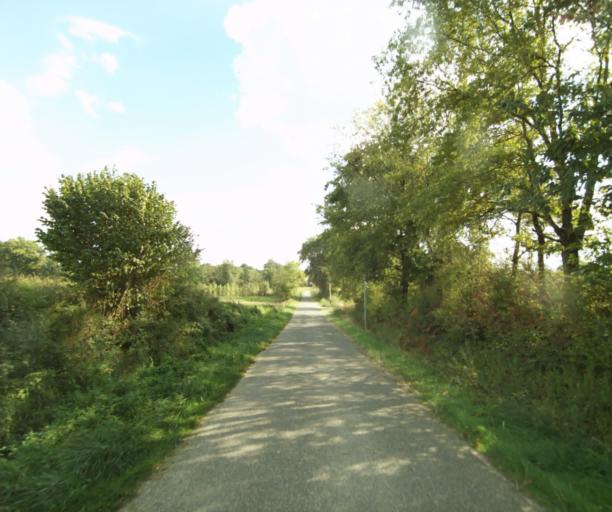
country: FR
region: Midi-Pyrenees
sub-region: Departement du Gers
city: Cazaubon
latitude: 43.8902
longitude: -0.0411
